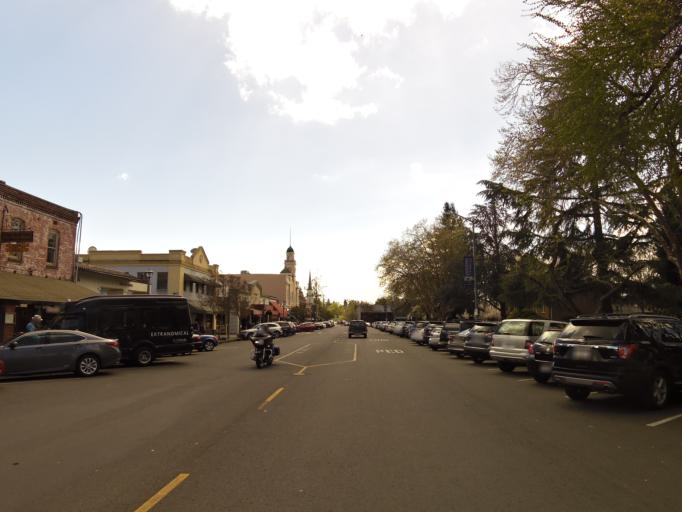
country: US
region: California
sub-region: Sonoma County
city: Sonoma
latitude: 38.2934
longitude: -122.4565
